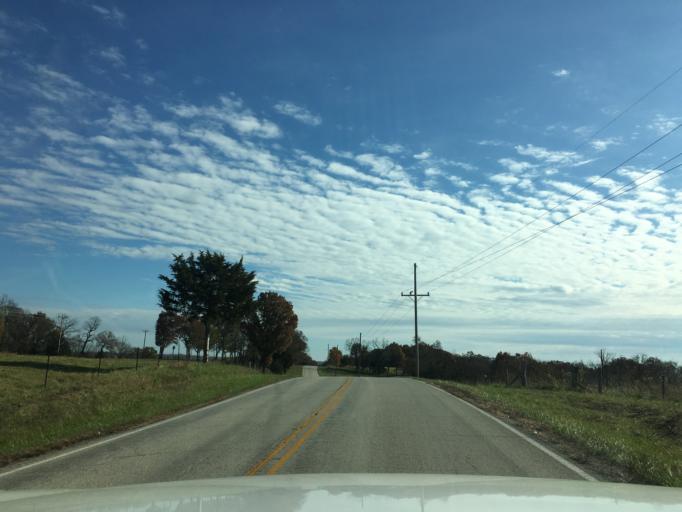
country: US
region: Missouri
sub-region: Osage County
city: Linn
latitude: 38.3758
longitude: -91.8155
